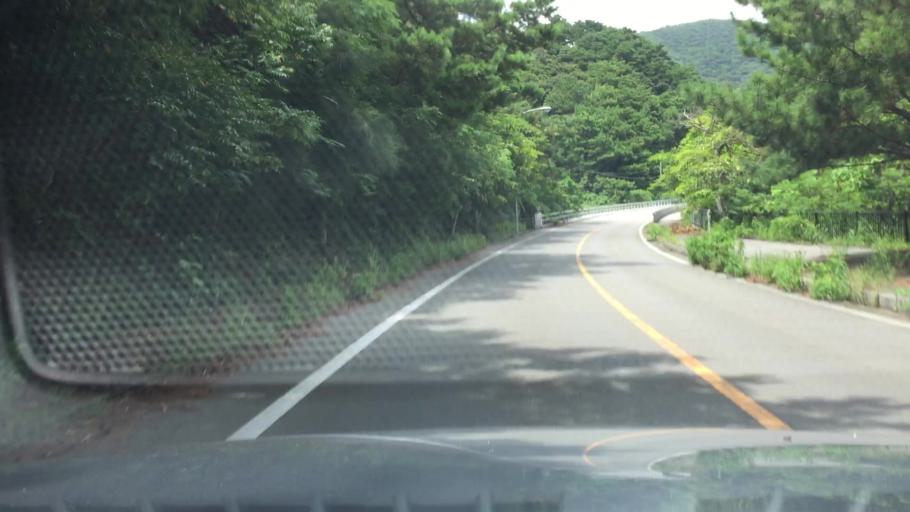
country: JP
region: Okinawa
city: Ishigaki
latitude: 24.4322
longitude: 124.2102
